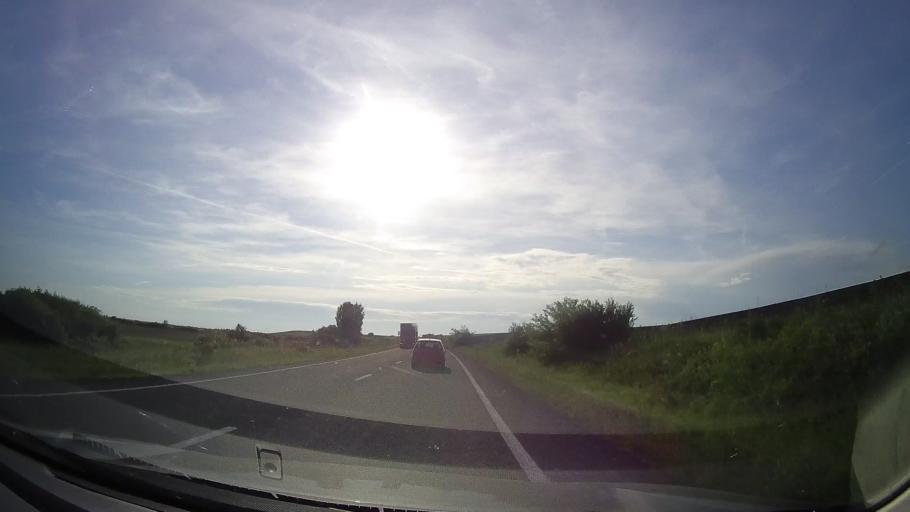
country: RO
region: Timis
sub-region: Oras Recas
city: Recas
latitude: 45.7938
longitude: 21.5540
